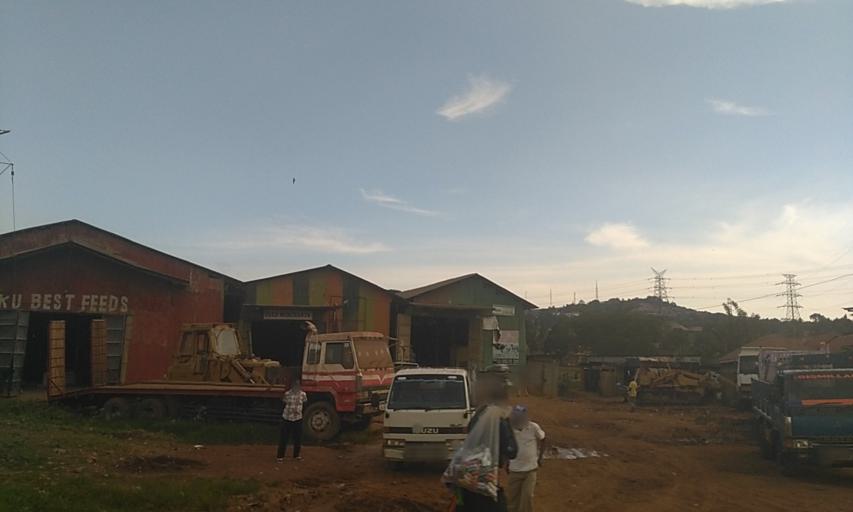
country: UG
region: Central Region
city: Kampala Central Division
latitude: 0.2984
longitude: 32.5299
